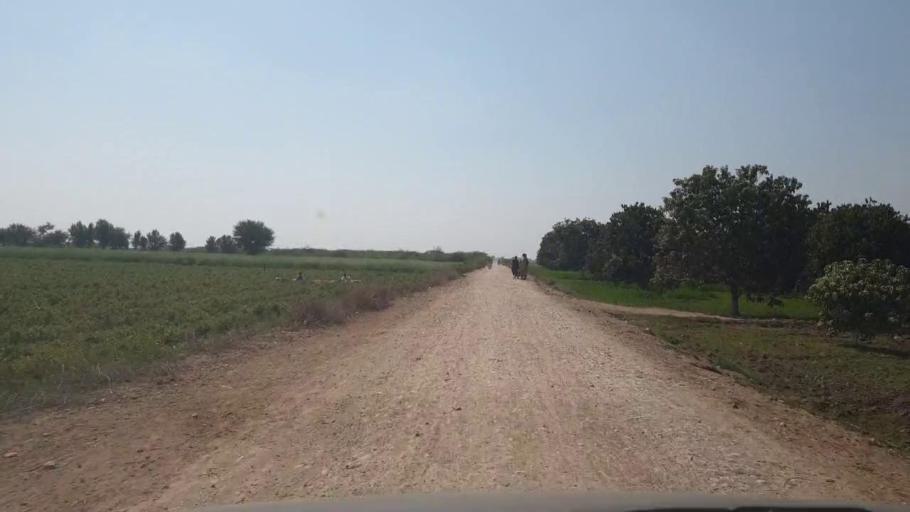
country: PK
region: Sindh
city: Digri
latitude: 25.2370
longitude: 69.2244
